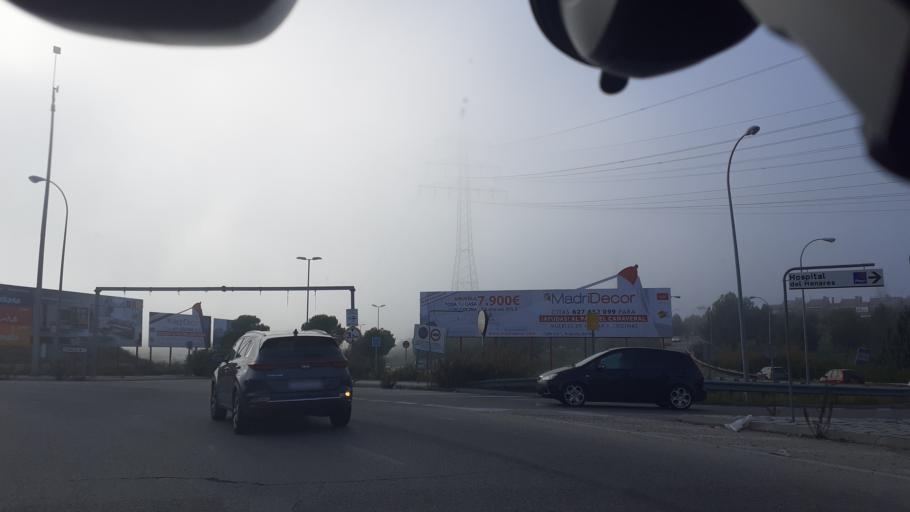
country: ES
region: Madrid
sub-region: Provincia de Madrid
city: Coslada
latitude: 40.4120
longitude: -3.5518
